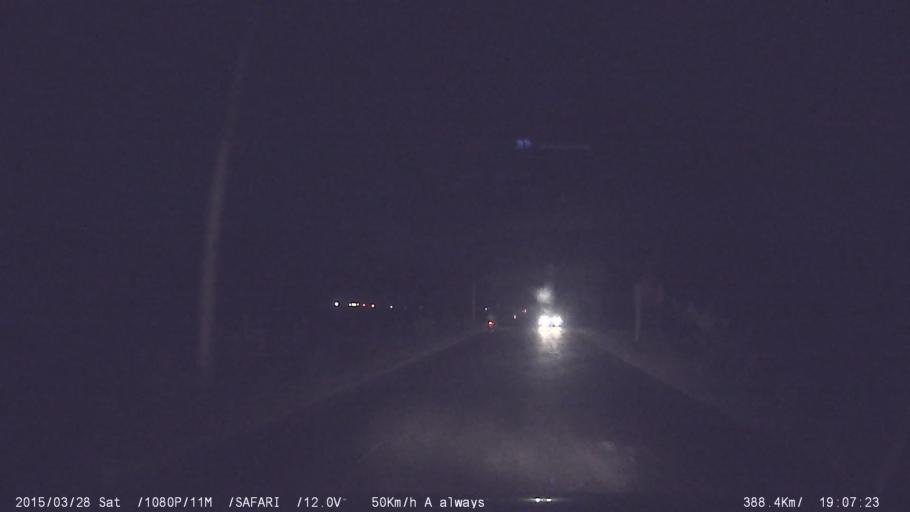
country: IN
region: Karnataka
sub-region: Mandya
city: Shrirangapattana
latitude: 12.3925
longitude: 76.6142
